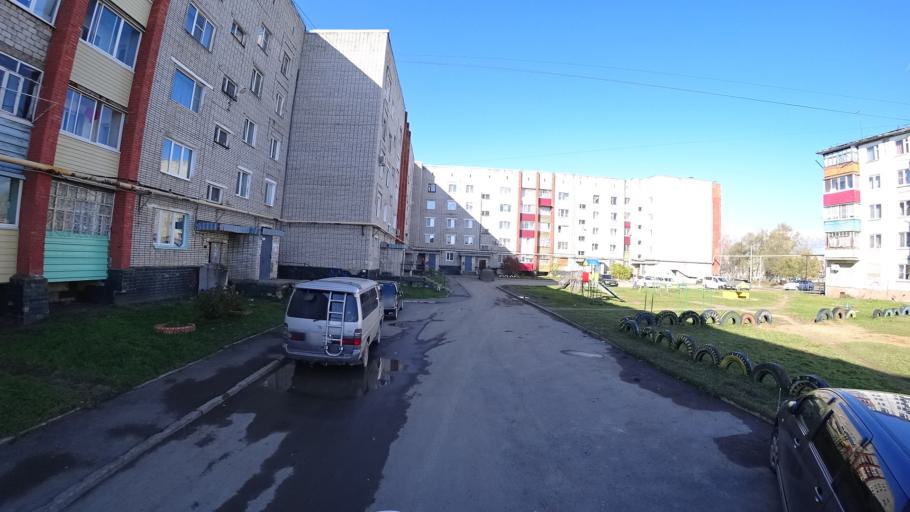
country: RU
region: Khabarovsk Krai
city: Amursk
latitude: 50.1004
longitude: 136.5143
